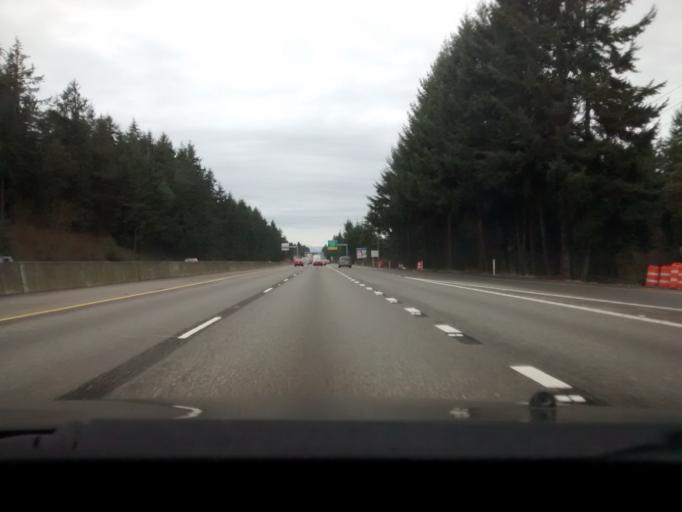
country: US
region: Washington
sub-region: Pierce County
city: Wollochet
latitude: 47.2949
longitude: -122.5672
